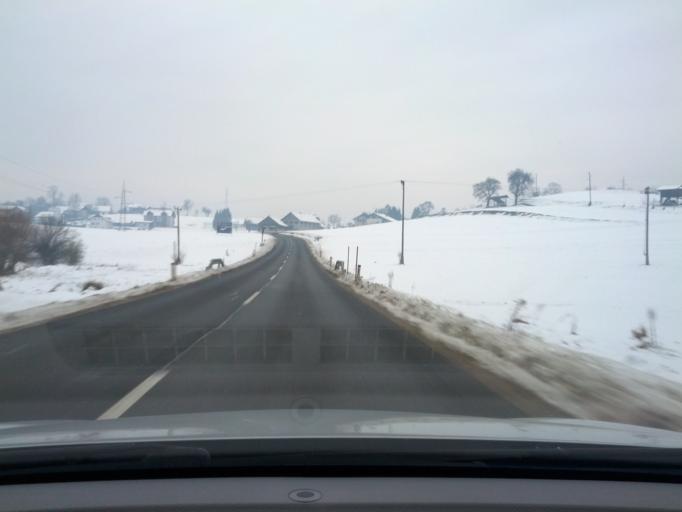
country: SI
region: Moravce
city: Moravce
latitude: 46.1376
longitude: 14.7237
